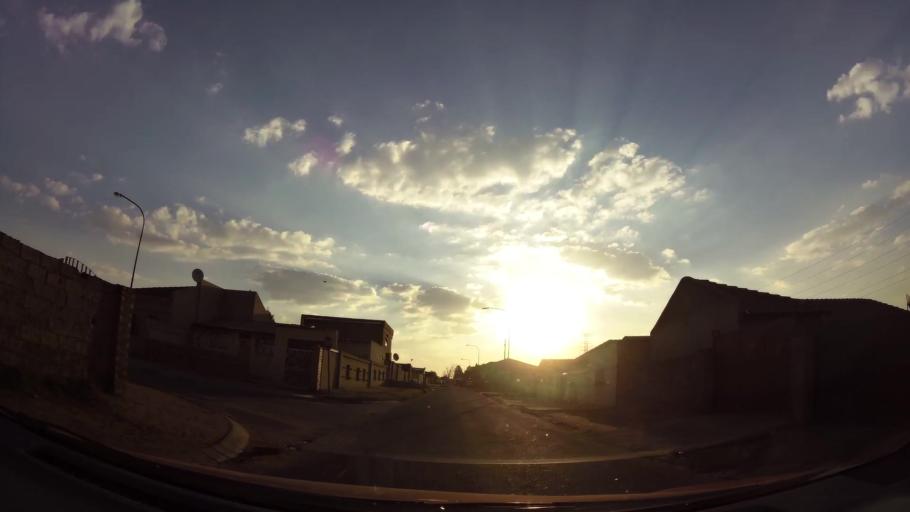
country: ZA
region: Gauteng
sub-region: City of Johannesburg Metropolitan Municipality
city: Roodepoort
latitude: -26.2097
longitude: 27.9016
